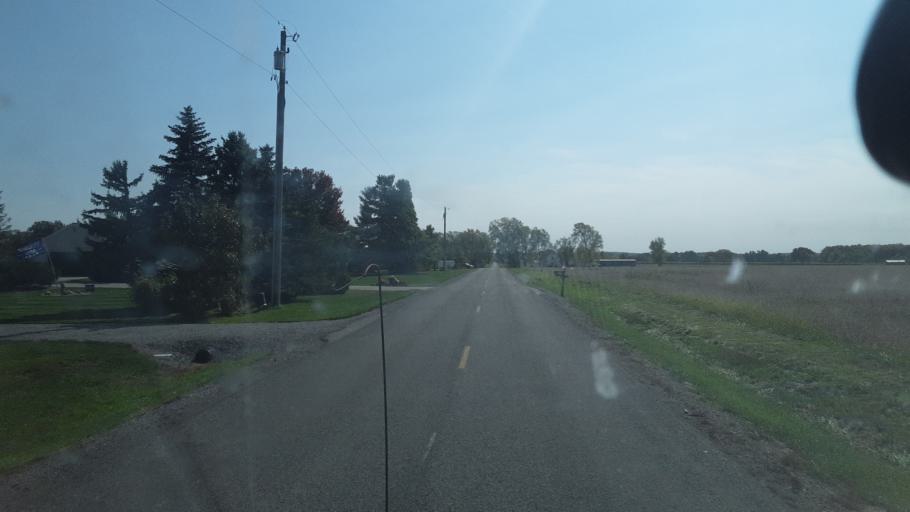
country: US
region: Ohio
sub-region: Logan County
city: Northwood
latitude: 40.5082
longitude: -83.7887
